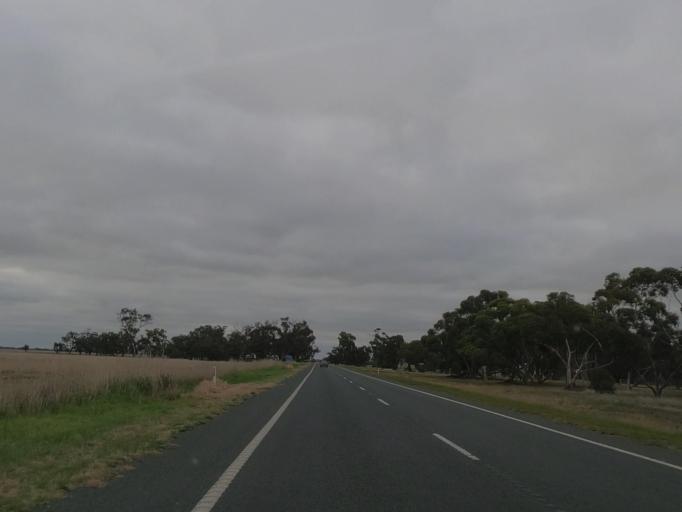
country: AU
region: Victoria
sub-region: Greater Bendigo
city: Long Gully
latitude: -36.2727
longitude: 143.9674
